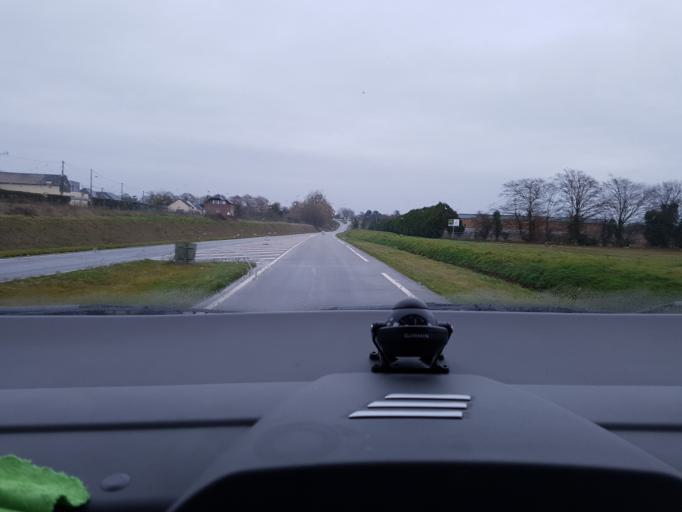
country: FR
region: Haute-Normandie
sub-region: Departement de l'Eure
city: Le Neubourg
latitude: 49.1410
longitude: 0.8943
